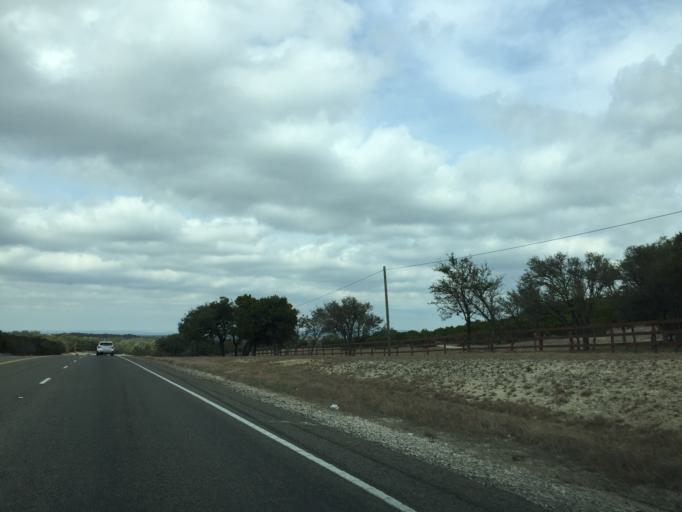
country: US
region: Texas
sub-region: Travis County
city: Briarcliff
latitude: 30.4386
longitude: -98.1446
